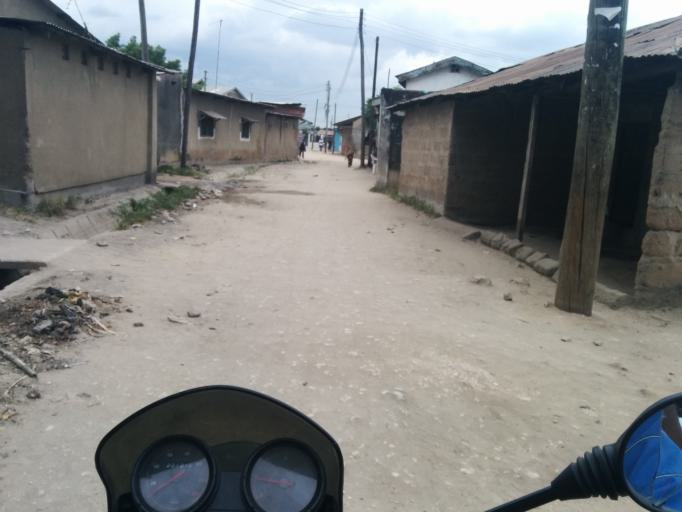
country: TZ
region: Dar es Salaam
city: Dar es Salaam
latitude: -6.8592
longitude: 39.2528
